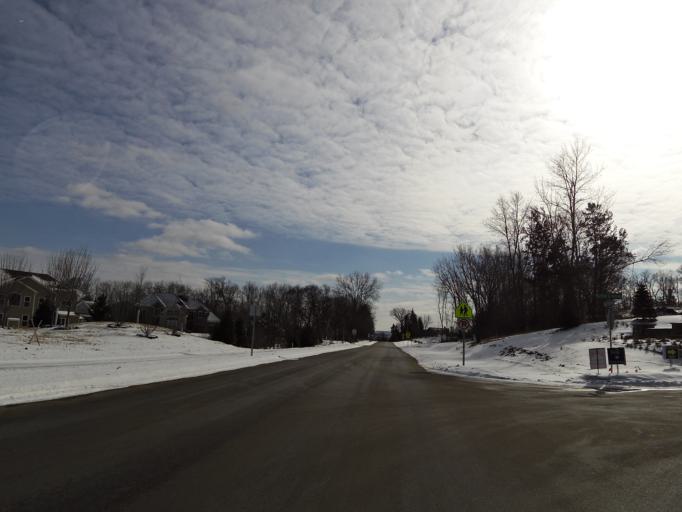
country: US
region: Minnesota
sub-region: Hennepin County
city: Eden Prairie
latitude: 44.8228
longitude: -93.4853
